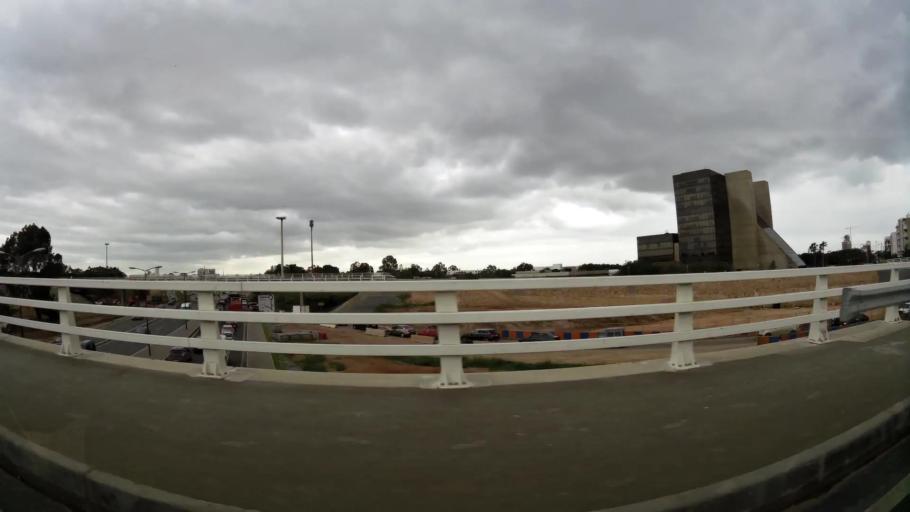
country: MA
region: Grand Casablanca
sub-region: Casablanca
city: Casablanca
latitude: 33.5491
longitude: -7.6440
